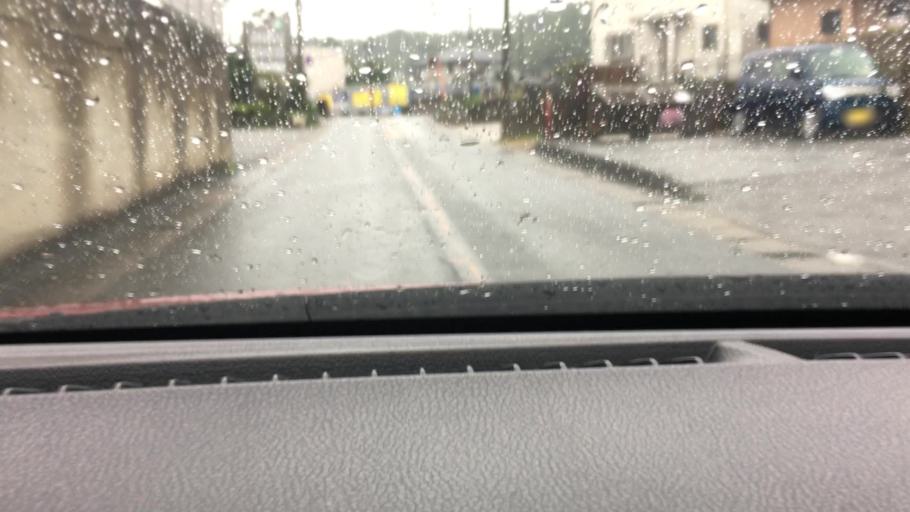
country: JP
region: Chiba
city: Kisarazu
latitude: 35.3730
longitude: 139.9397
